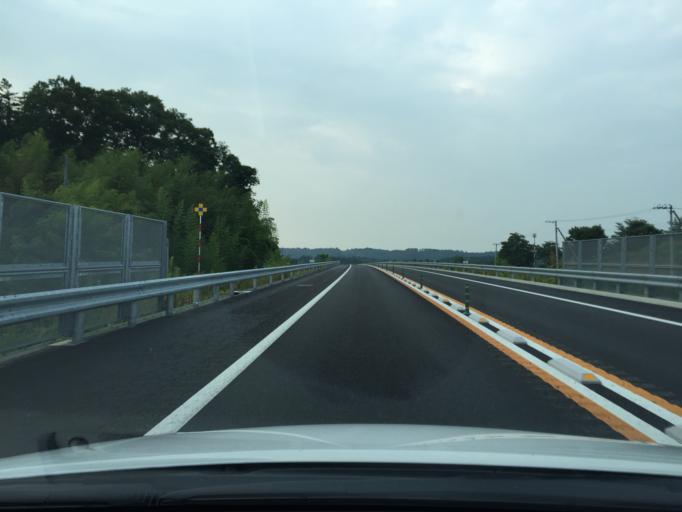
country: JP
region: Fukushima
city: Namie
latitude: 37.5647
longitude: 140.9450
